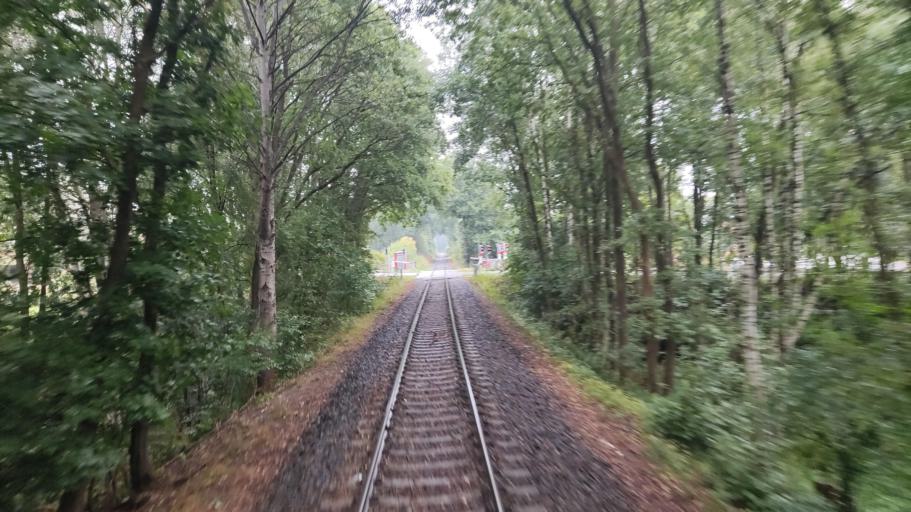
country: DE
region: Lower Saxony
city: Bispingen
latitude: 53.0891
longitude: 9.9974
